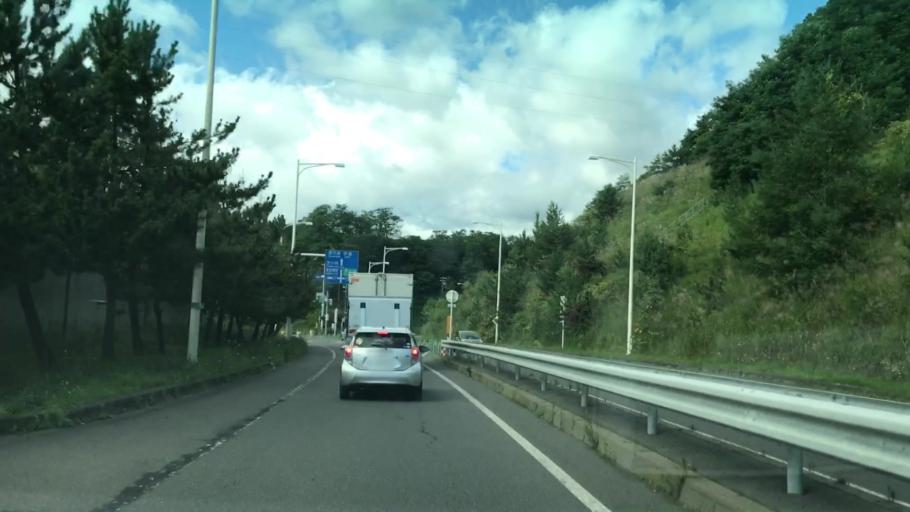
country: JP
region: Hokkaido
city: Muroran
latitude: 42.3642
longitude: 140.9520
